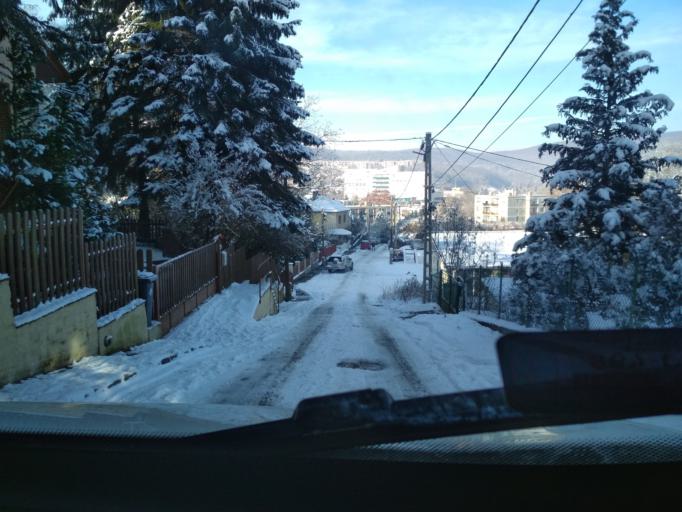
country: HU
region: Nograd
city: Salgotarjan
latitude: 48.1128
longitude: 19.8151
